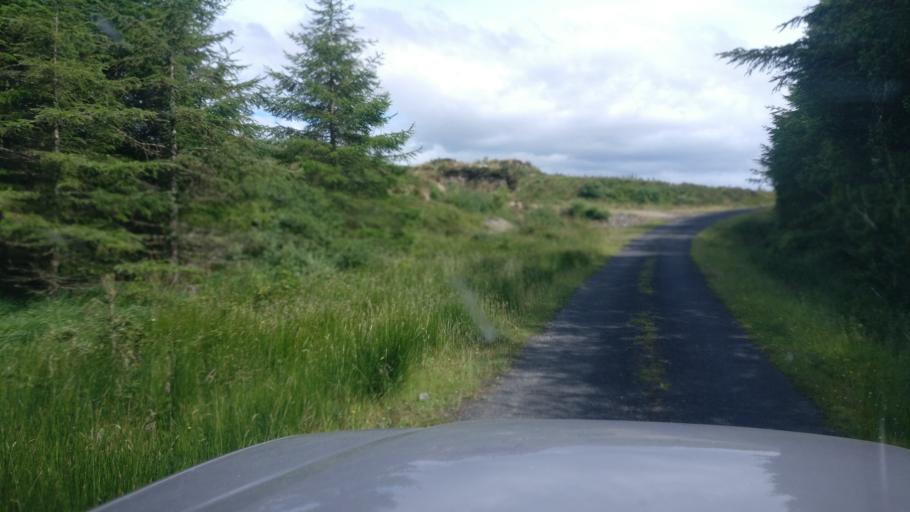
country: IE
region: Connaught
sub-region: County Galway
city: Gort
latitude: 53.0836
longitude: -8.6912
